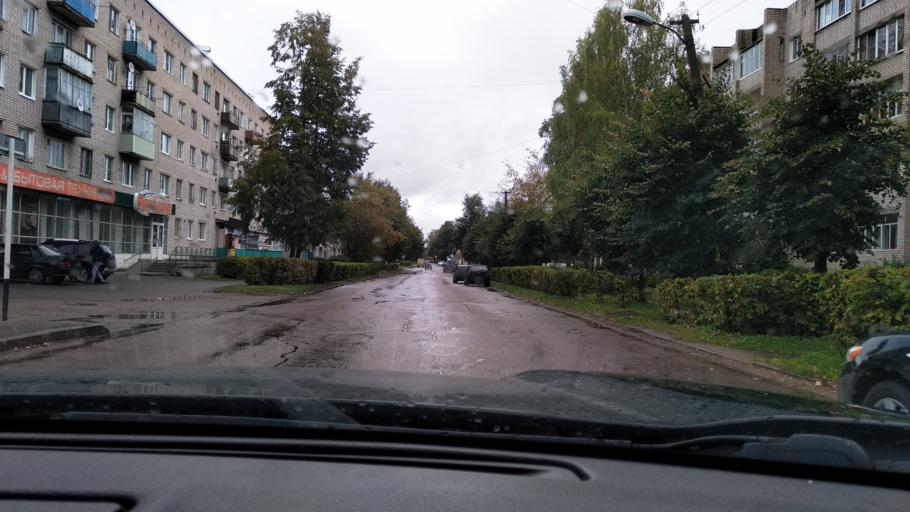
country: RU
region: Tverskaya
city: Kashin
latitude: 57.3559
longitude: 37.5967
